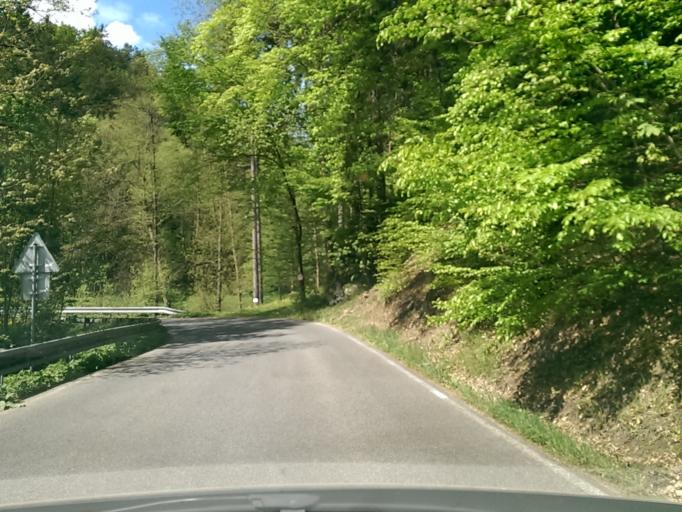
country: CZ
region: Liberecky
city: Mala Skala
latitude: 50.6590
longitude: 15.2154
